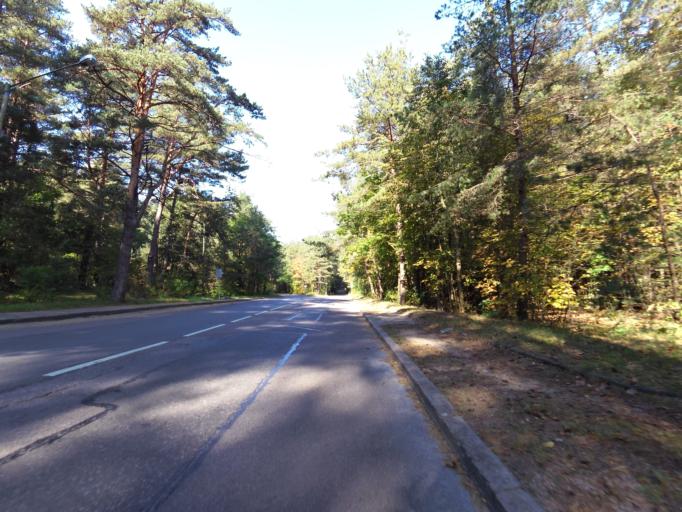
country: LT
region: Vilnius County
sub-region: Vilnius
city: Vilnius
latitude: 54.7307
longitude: 25.3093
